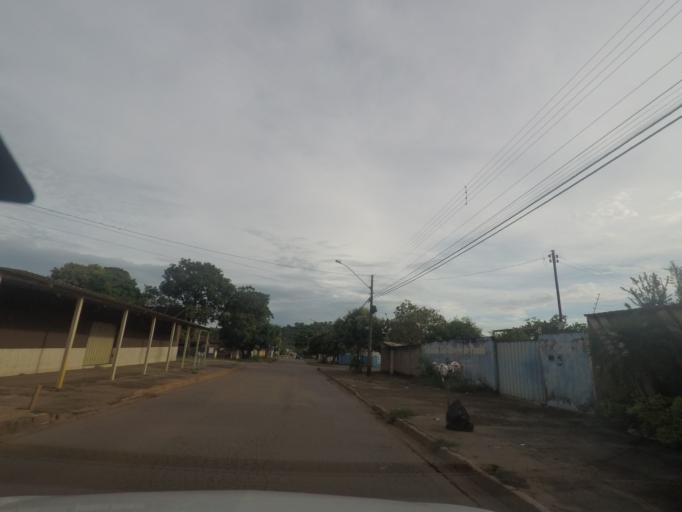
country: BR
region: Goias
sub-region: Goiania
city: Goiania
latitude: -16.6895
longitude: -49.3587
